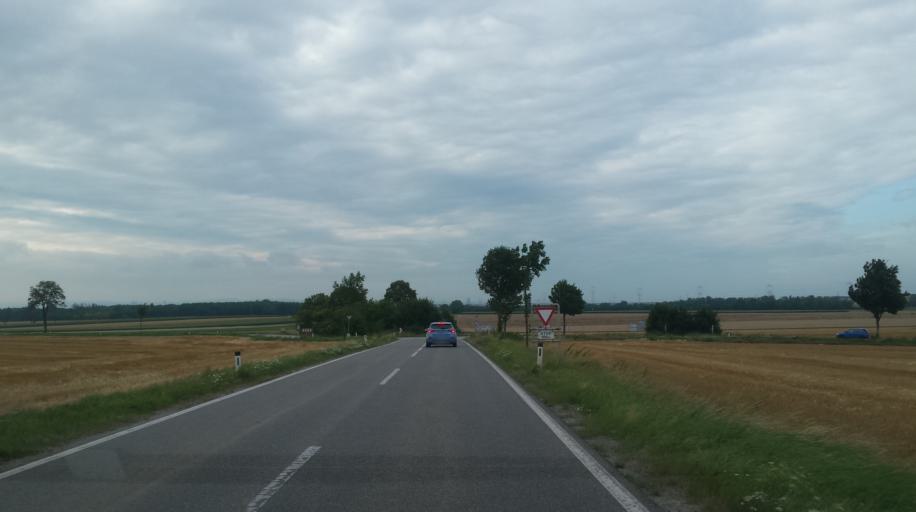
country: AT
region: Lower Austria
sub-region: Politischer Bezirk Wien-Umgebung
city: Moosbrunn
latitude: 48.0411
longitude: 16.4644
